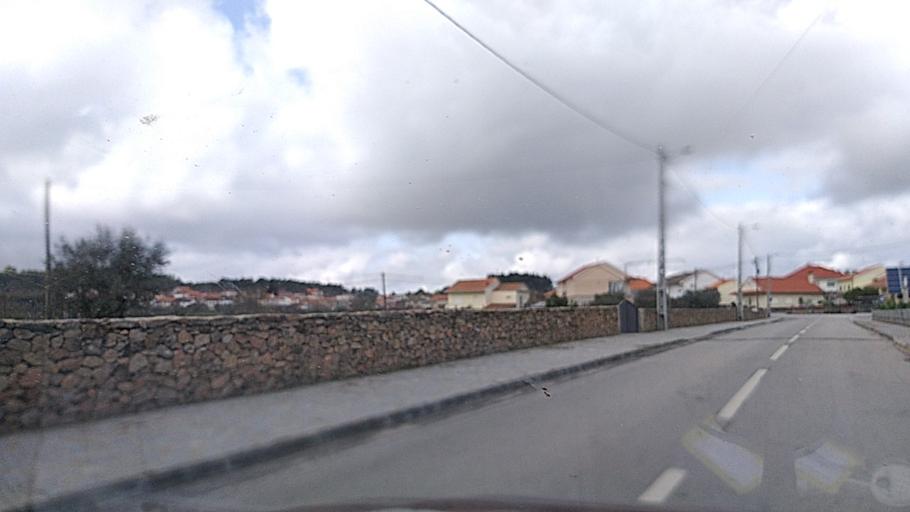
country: PT
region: Guarda
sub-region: Fornos de Algodres
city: Fornos de Algodres
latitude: 40.6610
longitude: -7.5616
